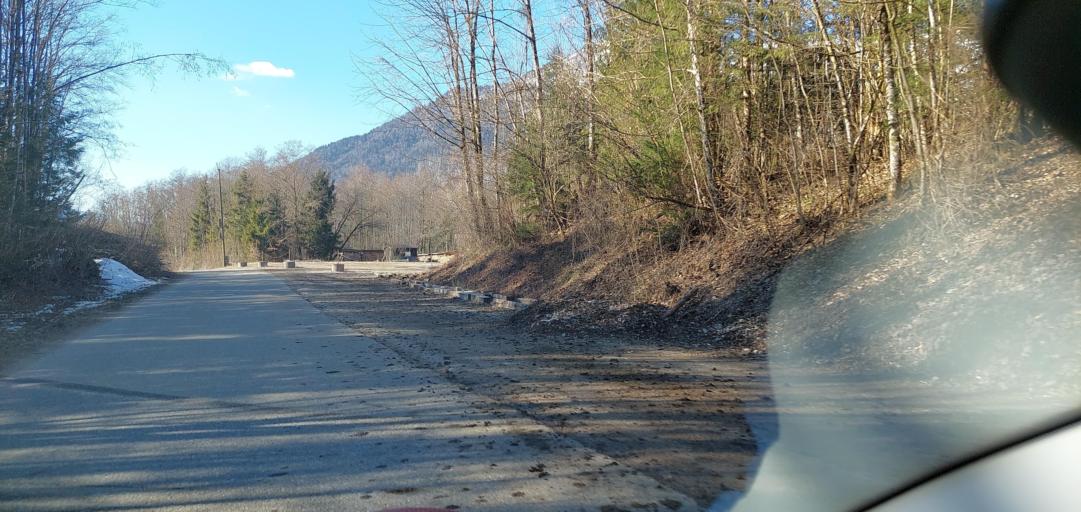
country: AT
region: Upper Austria
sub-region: Politischer Bezirk Gmunden
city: Bad Ischl
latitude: 47.7153
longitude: 13.5939
